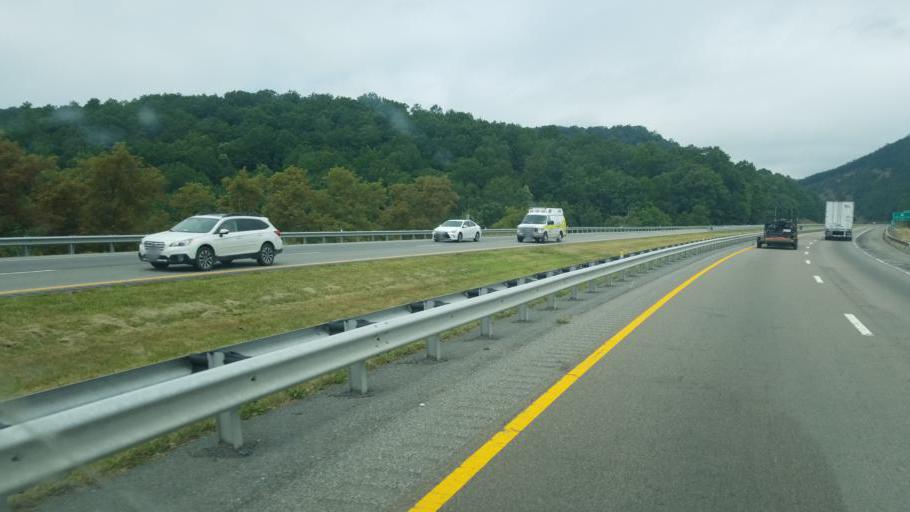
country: US
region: Virginia
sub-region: Wythe County
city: Wytheville
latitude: 37.0163
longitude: -81.1070
